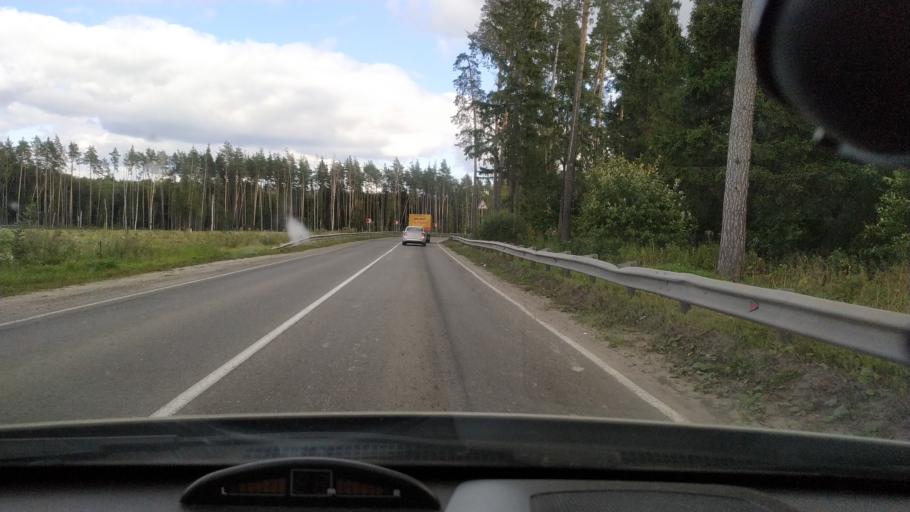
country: RU
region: Moskovskaya
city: Chornaya
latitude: 55.7694
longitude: 38.0546
